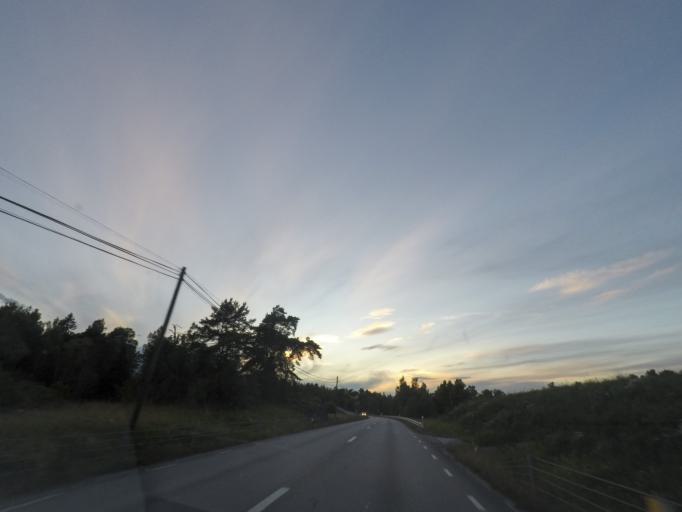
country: SE
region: Stockholm
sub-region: Sigtuna Kommun
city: Sigtuna
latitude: 59.6510
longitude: 17.7003
